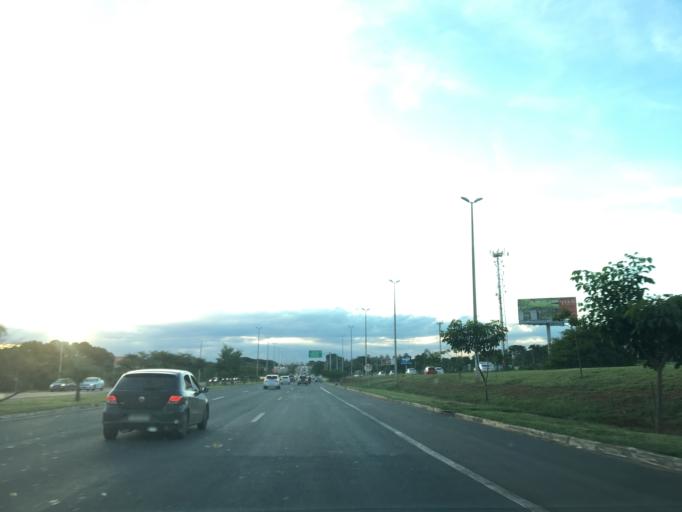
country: BR
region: Federal District
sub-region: Brasilia
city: Brasilia
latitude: -15.8427
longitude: -47.9461
